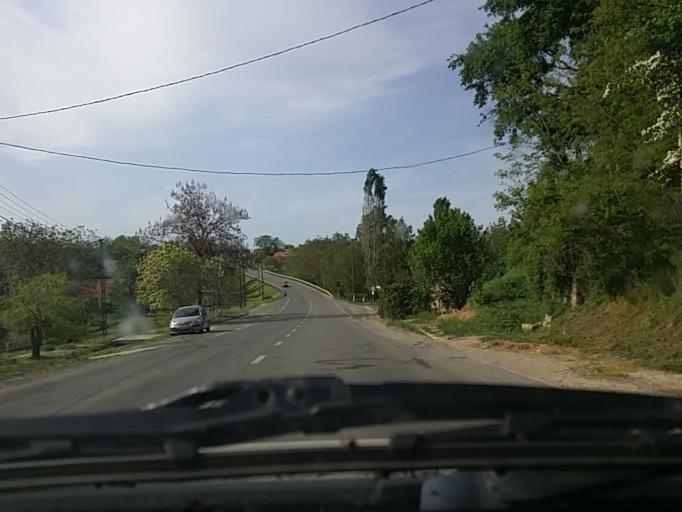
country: HU
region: Baranya
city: Harkany
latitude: 45.9047
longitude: 18.2307
